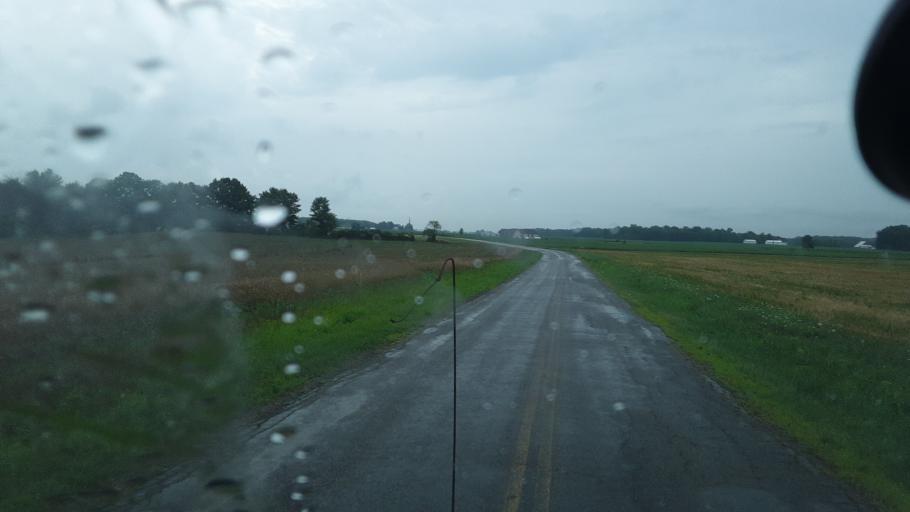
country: US
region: Ohio
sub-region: Williams County
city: Edgerton
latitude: 41.5243
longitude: -84.8006
